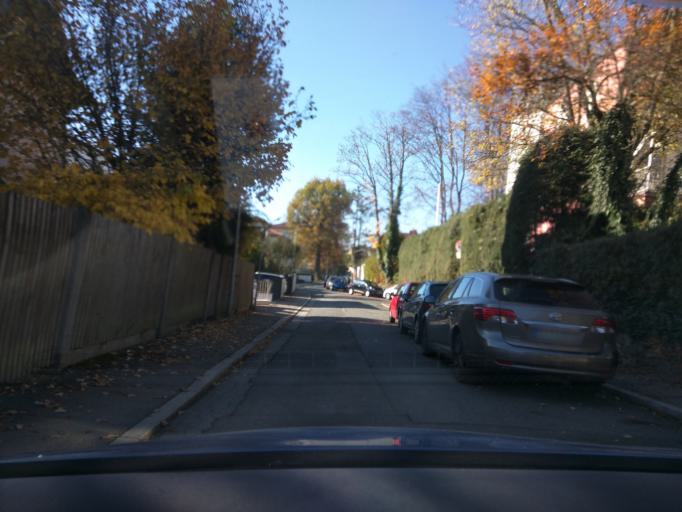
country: DE
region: Bavaria
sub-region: Lower Bavaria
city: Passau
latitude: 48.5693
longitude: 13.4471
